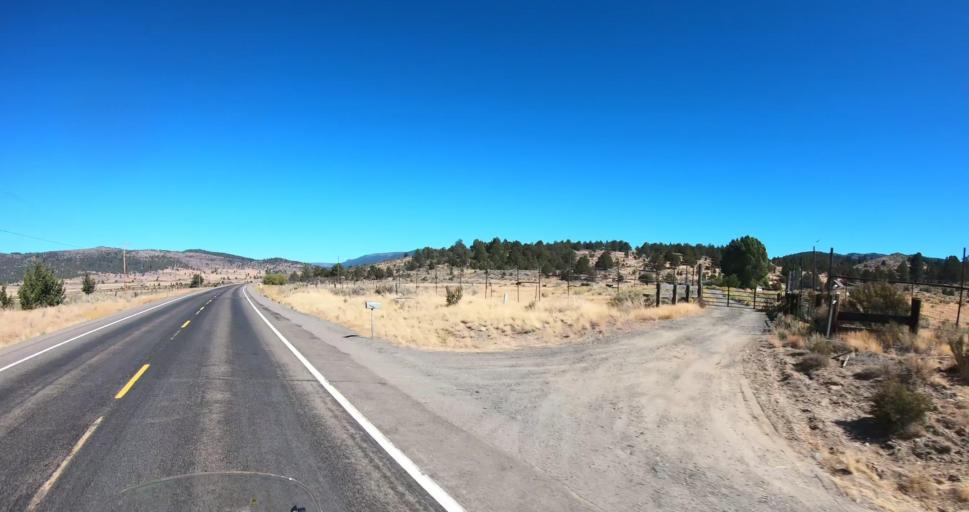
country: US
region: Oregon
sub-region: Lake County
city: Lakeview
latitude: 42.3120
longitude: -120.3395
